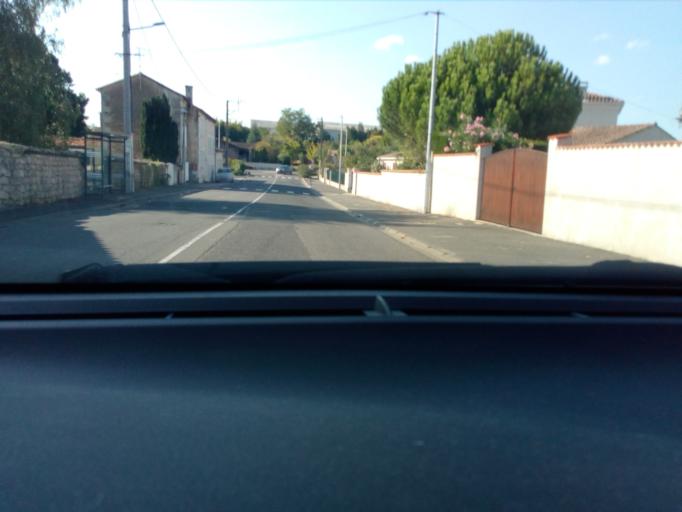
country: FR
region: Poitou-Charentes
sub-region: Departement de la Charente
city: Saint-Yrieix-sur-Charente
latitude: 45.6693
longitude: 0.1338
